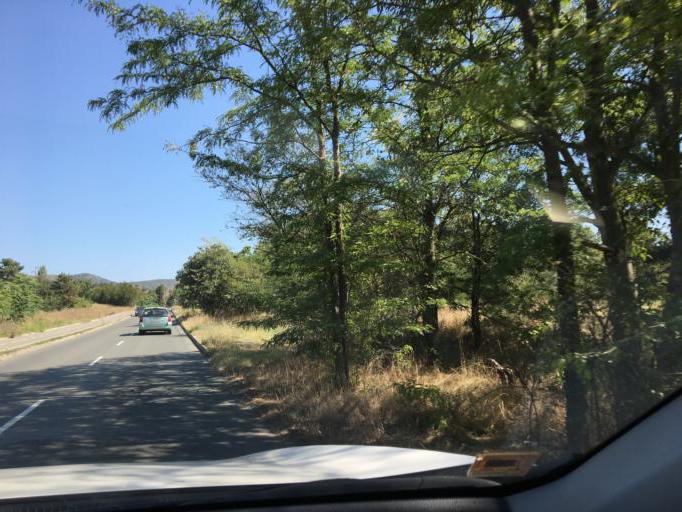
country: BG
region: Burgas
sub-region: Obshtina Kameno
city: Kameno
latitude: 42.6153
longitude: 27.3935
